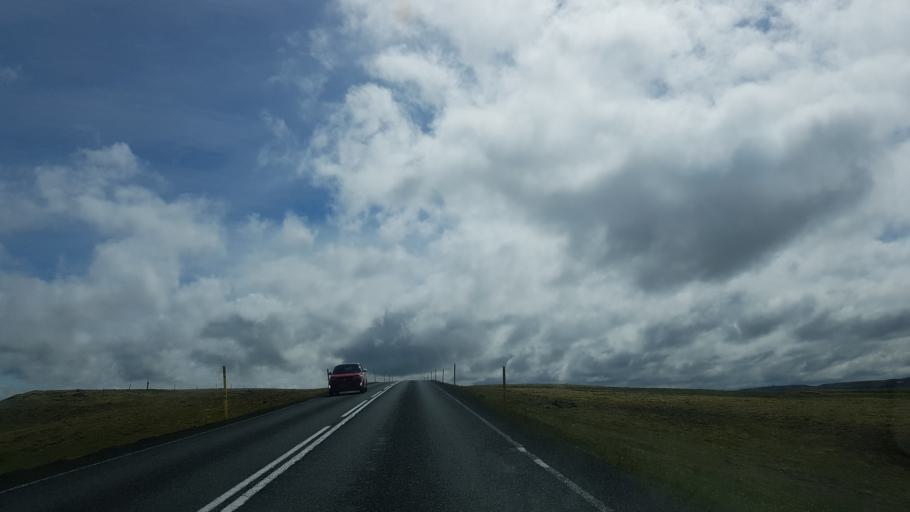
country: IS
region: West
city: Borgarnes
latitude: 65.0112
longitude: -21.0679
